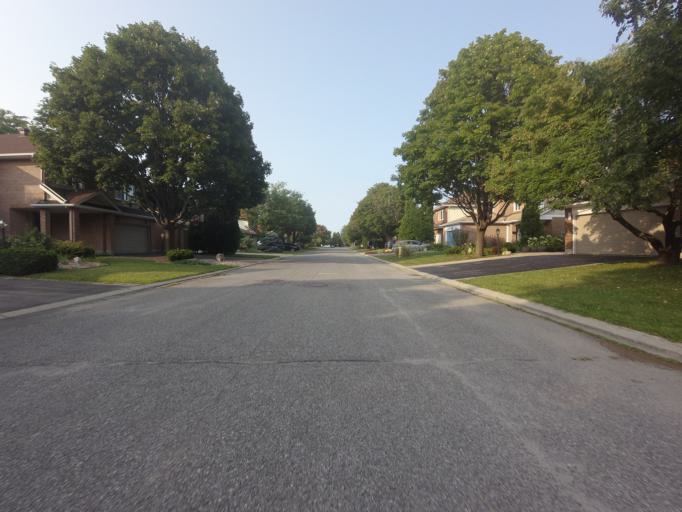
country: CA
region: Ontario
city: Bells Corners
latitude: 45.3372
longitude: -75.7713
